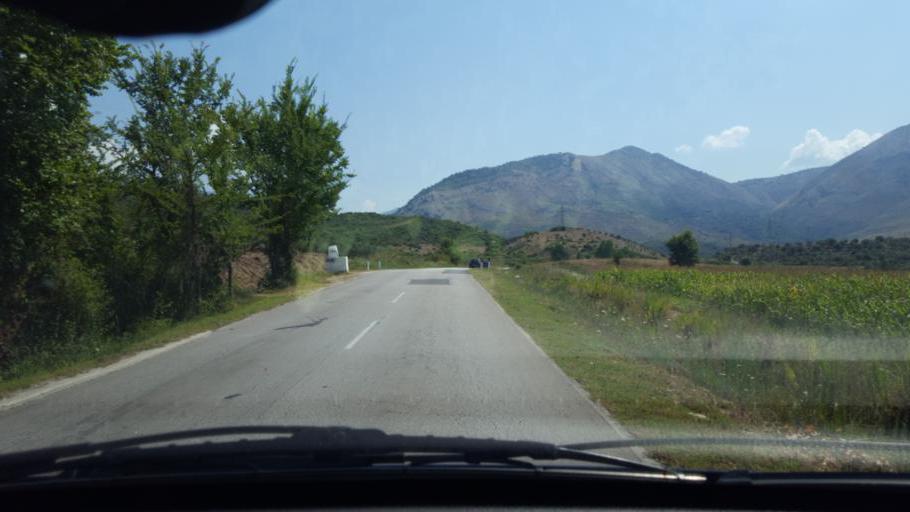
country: AL
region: Vlore
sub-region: Rrethi i Delvines
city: Mesopotam
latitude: 39.9119
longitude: 20.1103
